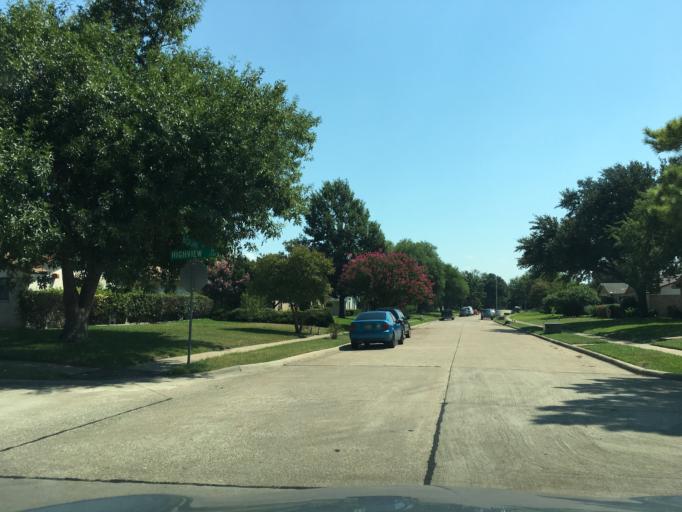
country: US
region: Texas
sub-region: Dallas County
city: Garland
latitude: 32.9412
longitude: -96.6610
